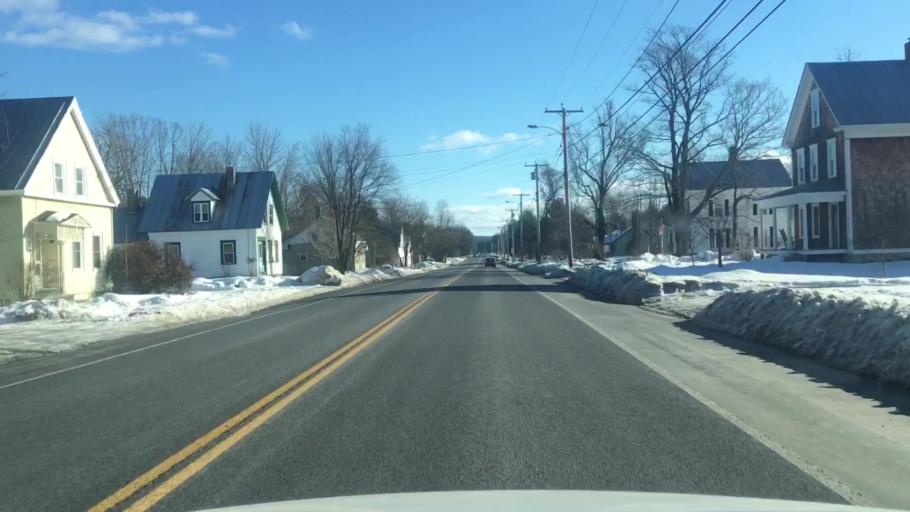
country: US
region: Maine
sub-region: Somerset County
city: Madison
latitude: 44.9481
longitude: -69.8574
